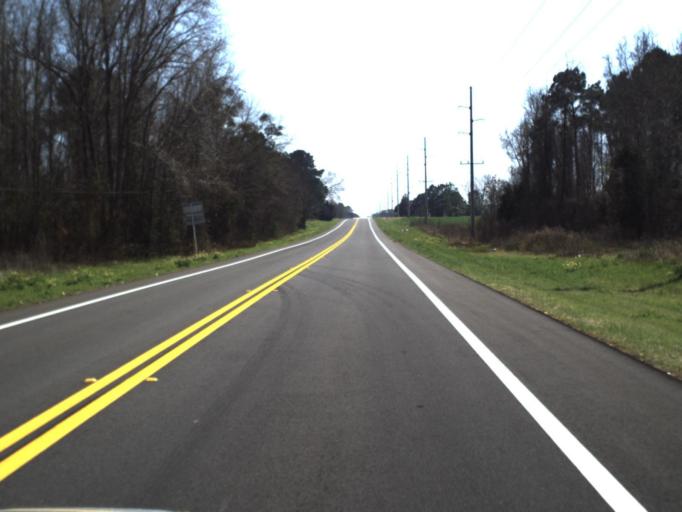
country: US
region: Florida
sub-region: Jackson County
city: Sneads
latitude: 30.8133
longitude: -85.0417
